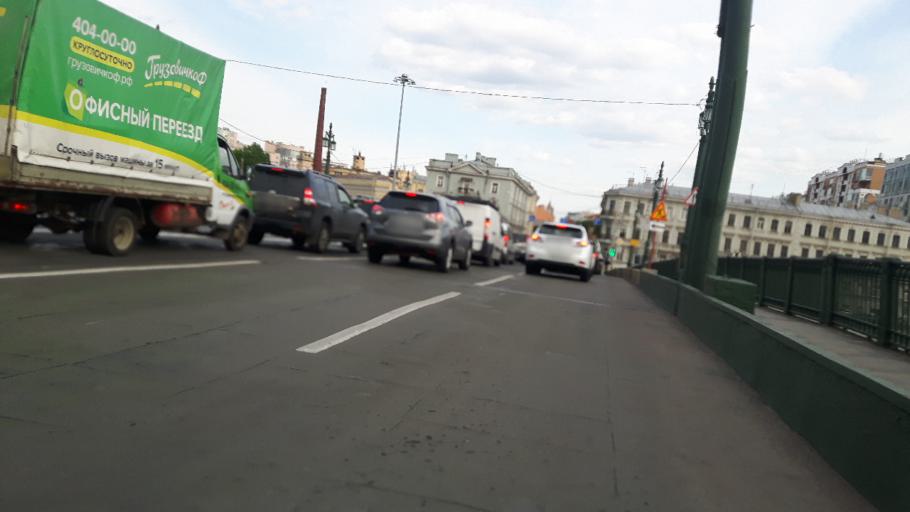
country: RU
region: St.-Petersburg
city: Novaya Derevnya
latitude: 59.9671
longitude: 30.2800
